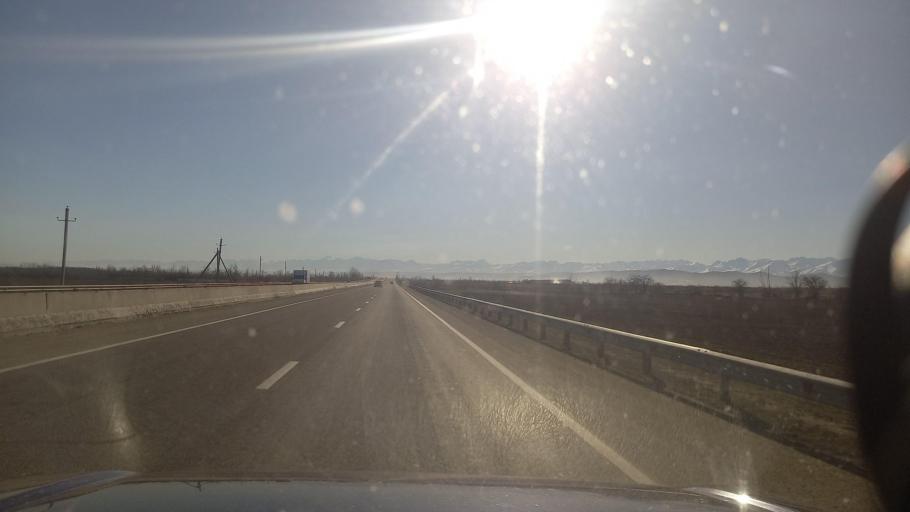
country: RU
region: Kabardino-Balkariya
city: Kishpek
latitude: 43.6078
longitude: 43.6574
